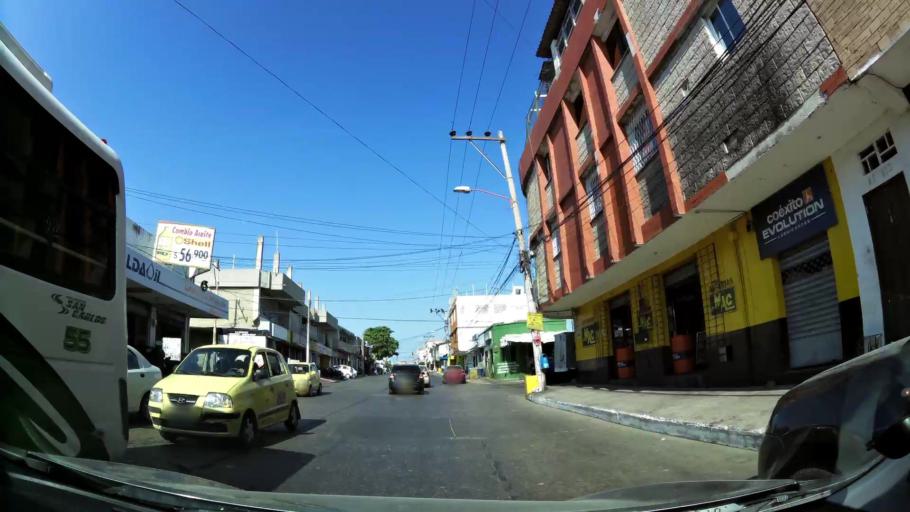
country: CO
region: Atlantico
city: Barranquilla
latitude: 10.9804
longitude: -74.7891
